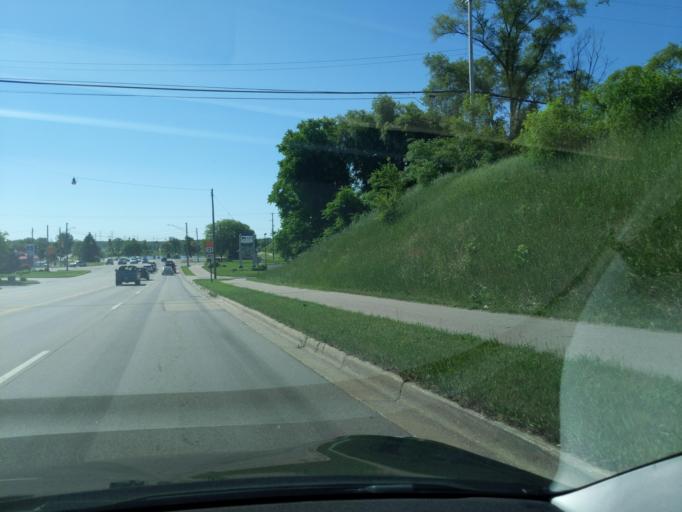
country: US
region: Michigan
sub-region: Muskegon County
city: North Muskegon
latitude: 43.2669
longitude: -86.2512
